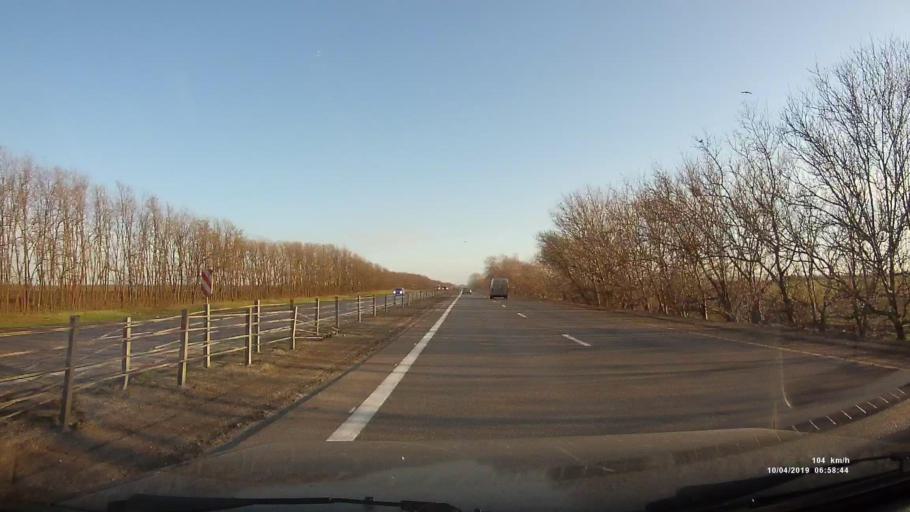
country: RU
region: Rostov
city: Grushevskaya
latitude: 47.5560
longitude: 39.9678
